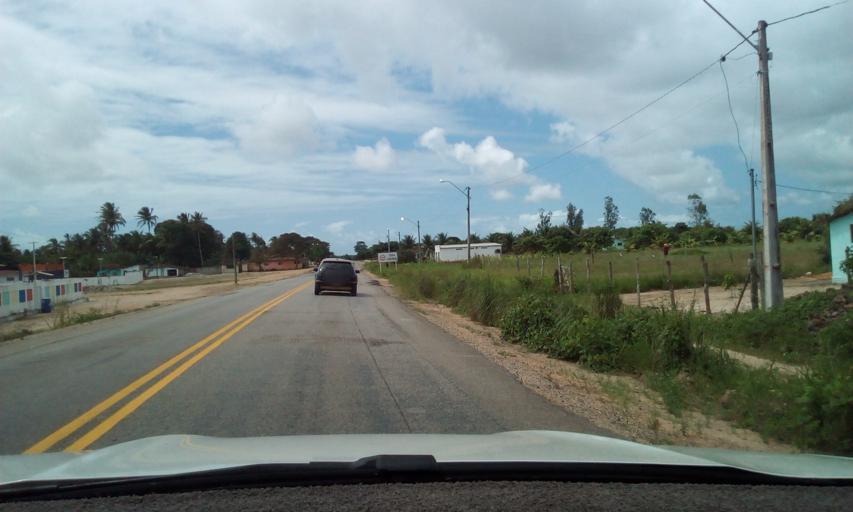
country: BR
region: Paraiba
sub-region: Rio Tinto
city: Rio Tinto
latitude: -6.7697
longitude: -35.0213
